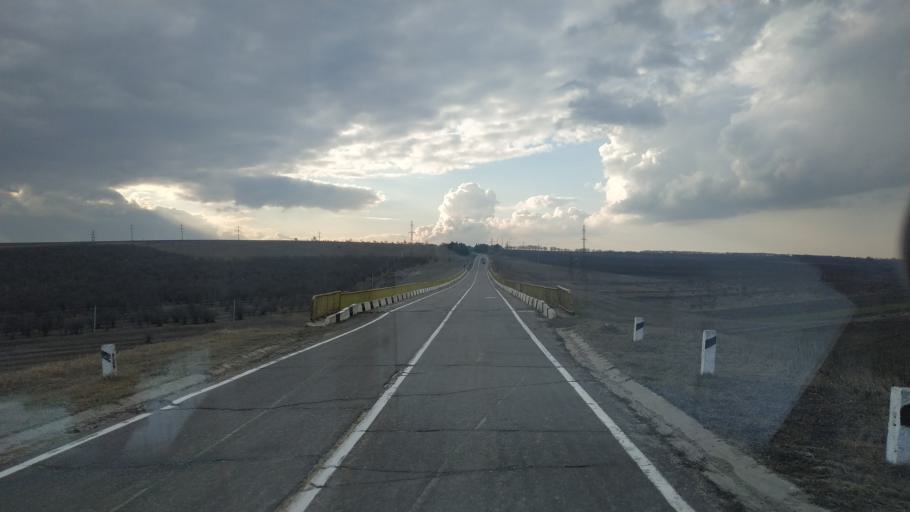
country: MD
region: Anenii Noi
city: Anenii Noi
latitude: 46.9257
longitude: 29.3041
